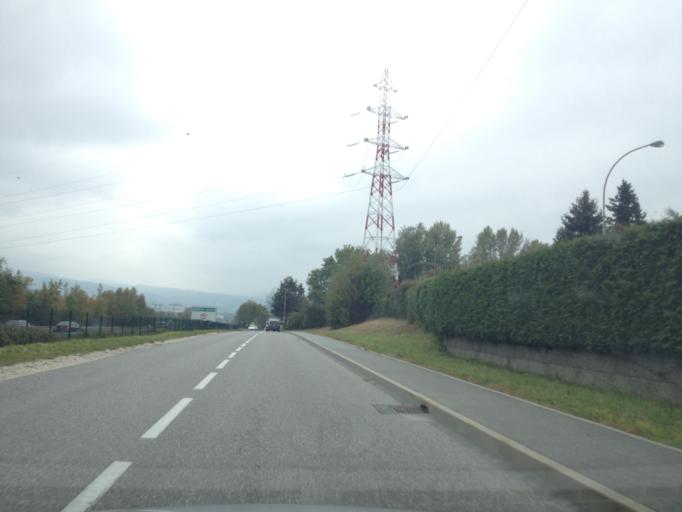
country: FR
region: Rhone-Alpes
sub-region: Departement de la Haute-Savoie
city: Seynod
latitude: 45.8878
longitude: 6.0837
